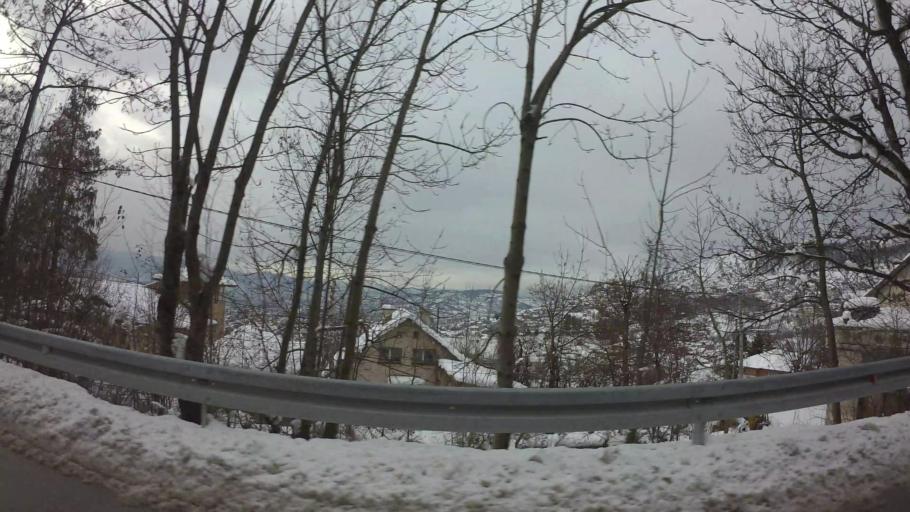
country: BA
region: Federation of Bosnia and Herzegovina
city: Kobilja Glava
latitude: 43.8707
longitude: 18.4412
